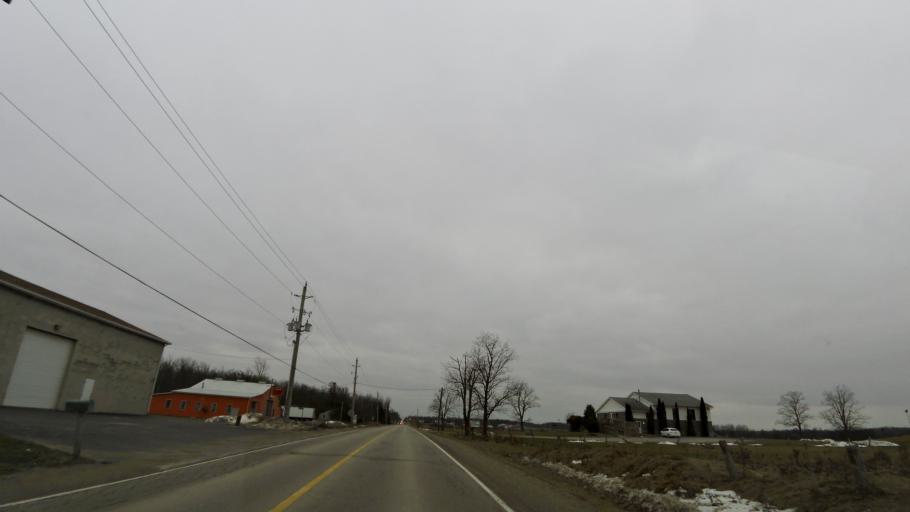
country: CA
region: Ontario
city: Brantford
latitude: 43.0891
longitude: -80.1047
